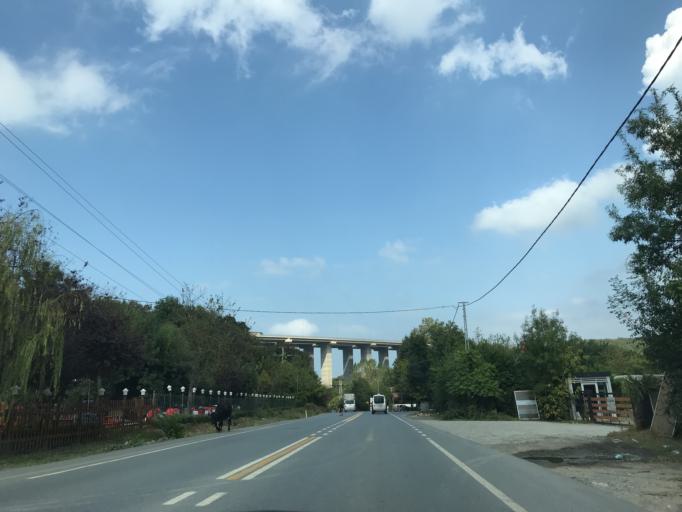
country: TR
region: Istanbul
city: Arikoey
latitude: 41.2224
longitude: 29.0341
